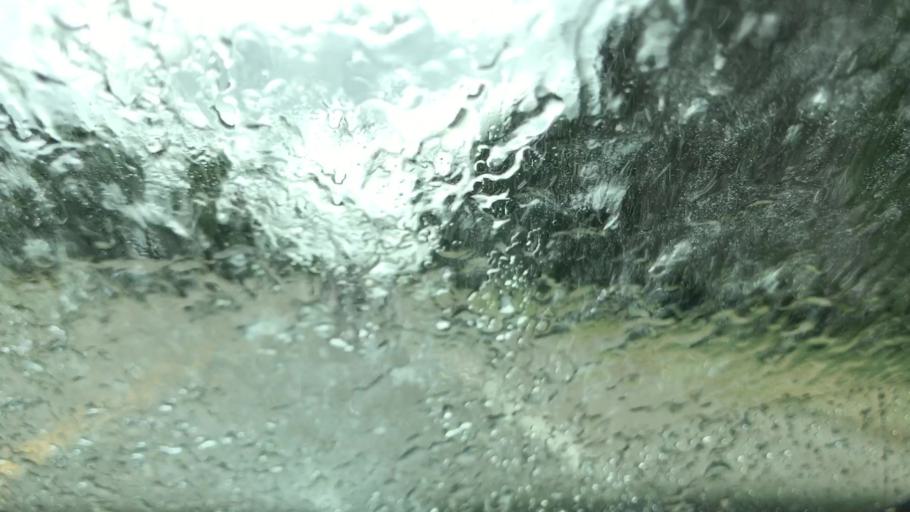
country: US
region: Michigan
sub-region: Muskegon County
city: Fruitport
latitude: 43.0741
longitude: -86.0944
